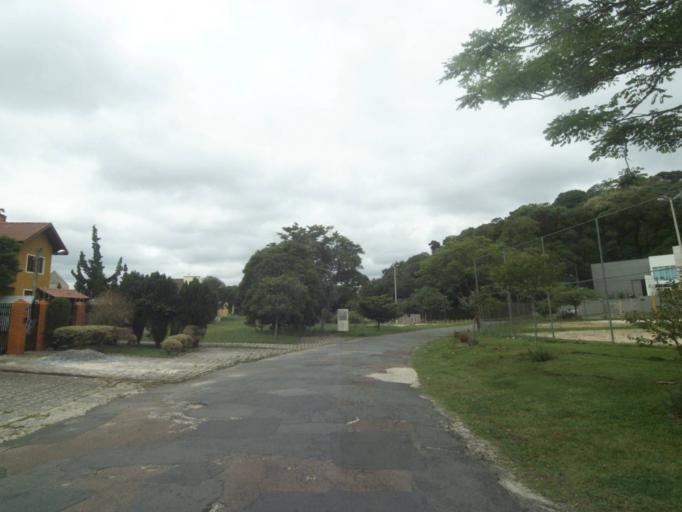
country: BR
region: Parana
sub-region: Curitiba
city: Curitiba
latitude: -25.3919
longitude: -49.2756
